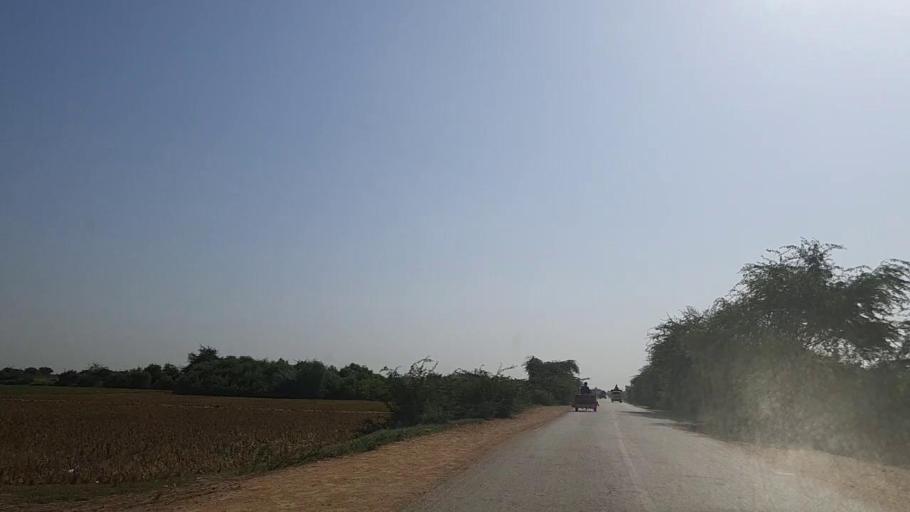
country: PK
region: Sindh
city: Mirpur Batoro
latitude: 24.6078
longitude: 68.2962
